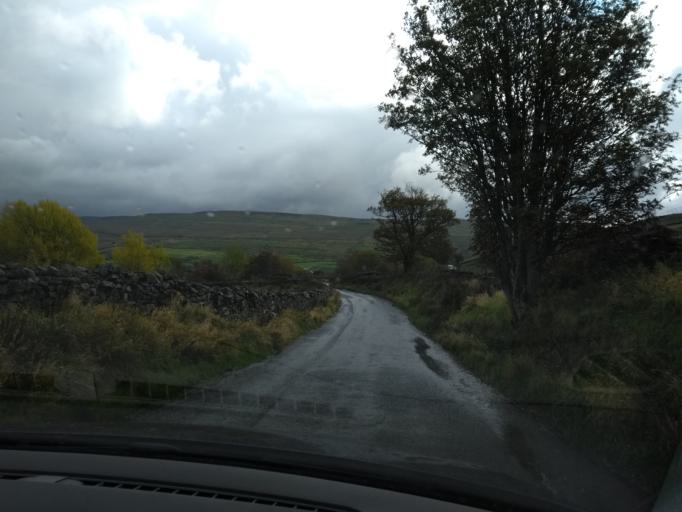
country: GB
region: England
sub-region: Cumbria
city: Kirkby Stephen
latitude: 54.3881
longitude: -2.1738
